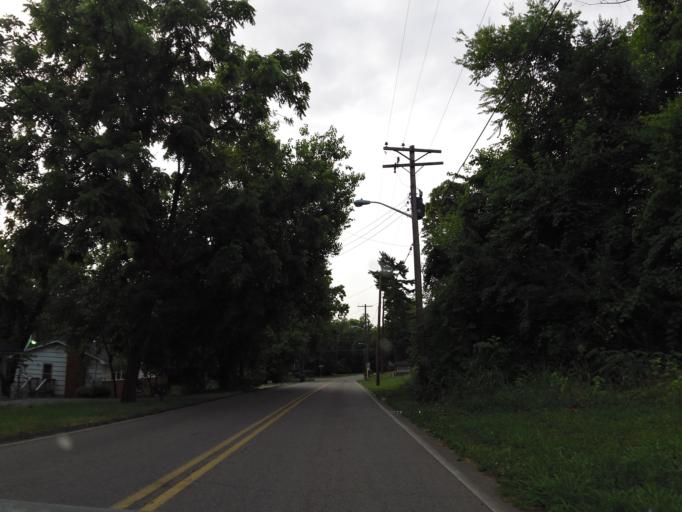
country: US
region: Tennessee
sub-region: Knox County
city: Knoxville
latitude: 35.9798
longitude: -83.8867
